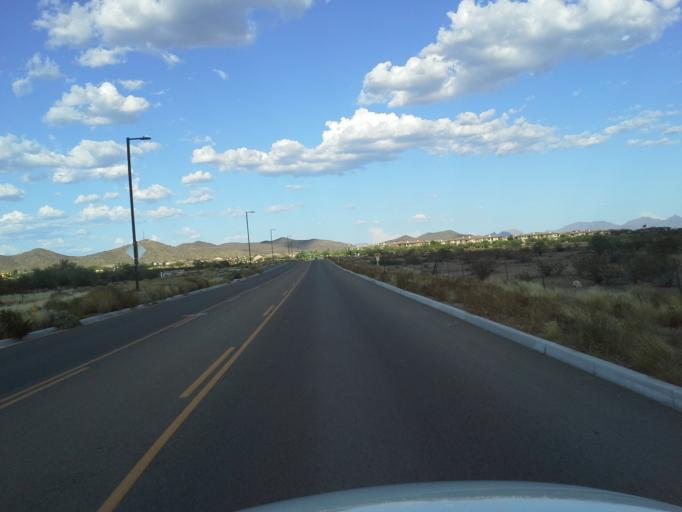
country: US
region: Arizona
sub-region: Maricopa County
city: Anthem
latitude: 33.7838
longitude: -112.1232
